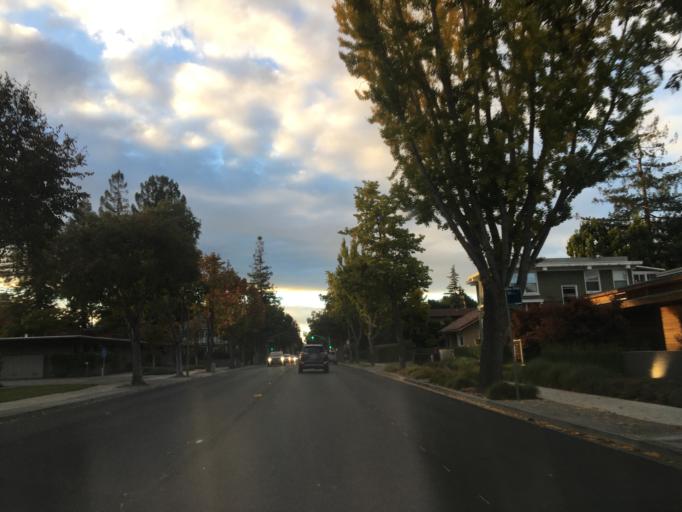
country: US
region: California
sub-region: Santa Clara County
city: Palo Alto
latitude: 37.4476
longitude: -122.1518
